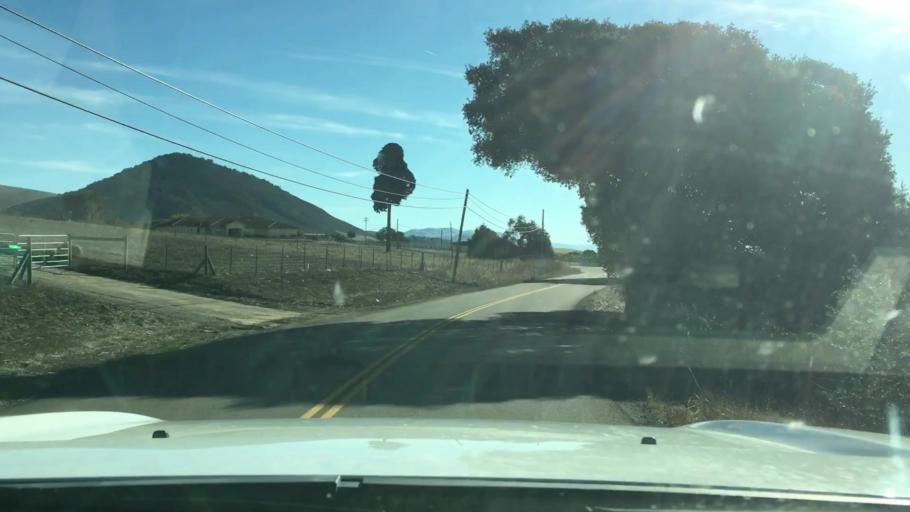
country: US
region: California
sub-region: San Luis Obispo County
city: Arroyo Grande
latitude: 35.1054
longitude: -120.5597
